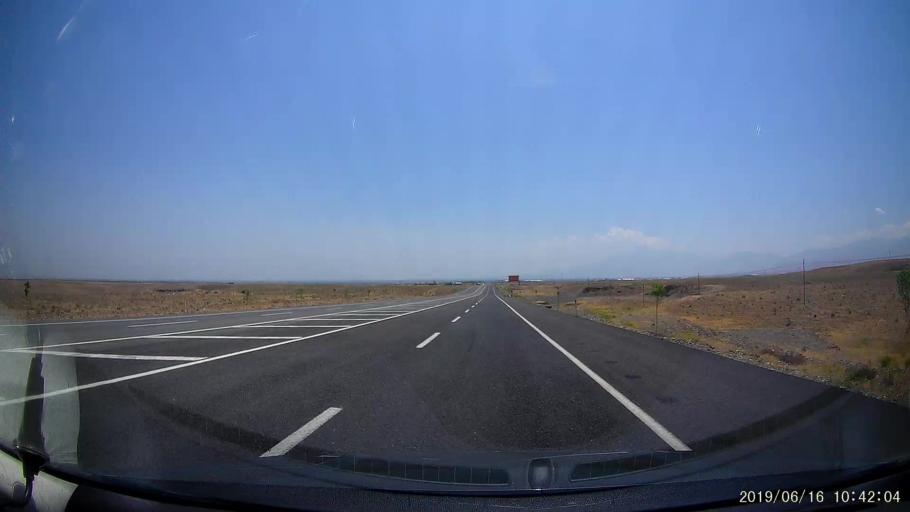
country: AM
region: Armavir
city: Shenavan
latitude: 40.0448
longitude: 43.7982
